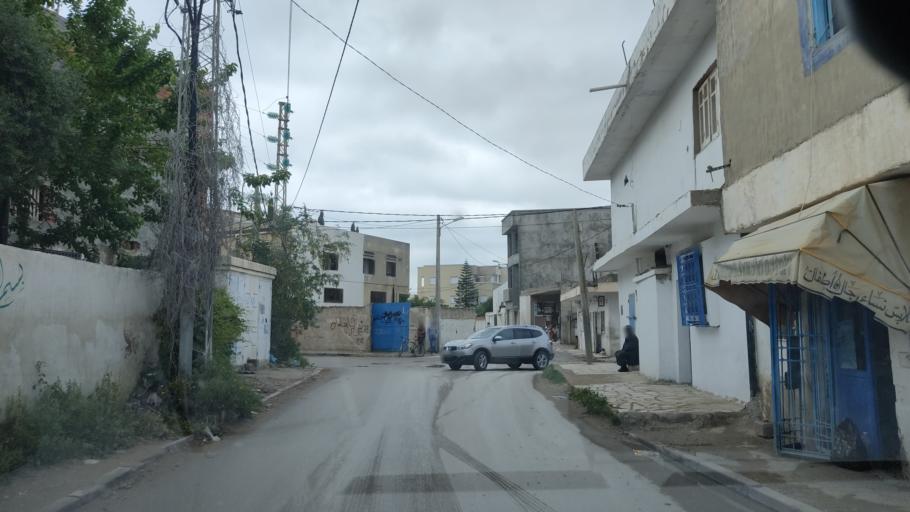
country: TN
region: Ariana
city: Ariana
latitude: 36.8774
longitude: 10.2172
